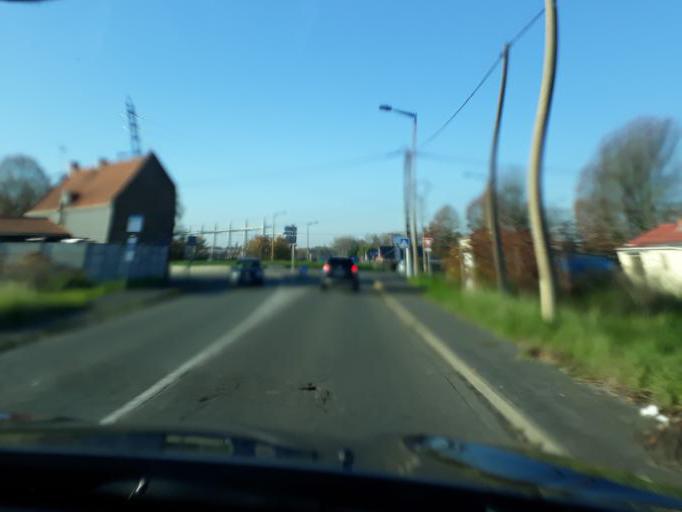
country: FR
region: Nord-Pas-de-Calais
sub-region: Departement du Nord
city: Sin-le-Noble
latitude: 50.3621
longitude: 3.1417
